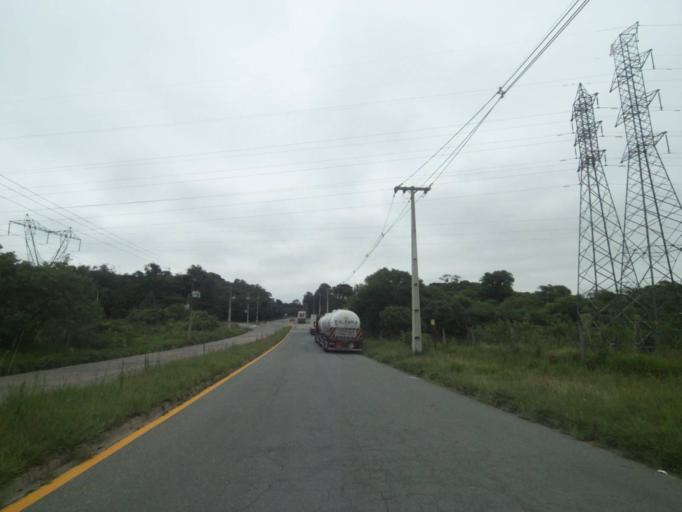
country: BR
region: Parana
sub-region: Araucaria
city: Araucaria
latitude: -25.5406
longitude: -49.3209
